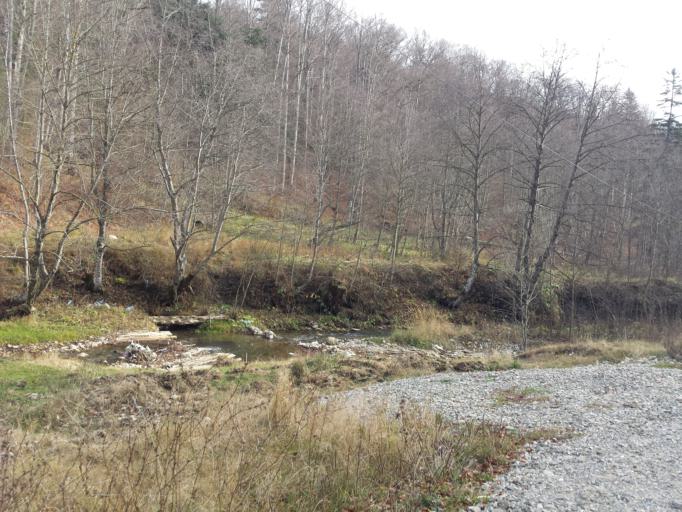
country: RO
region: Prahova
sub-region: Oras Azuga
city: Azuga
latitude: 45.4276
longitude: 25.5371
